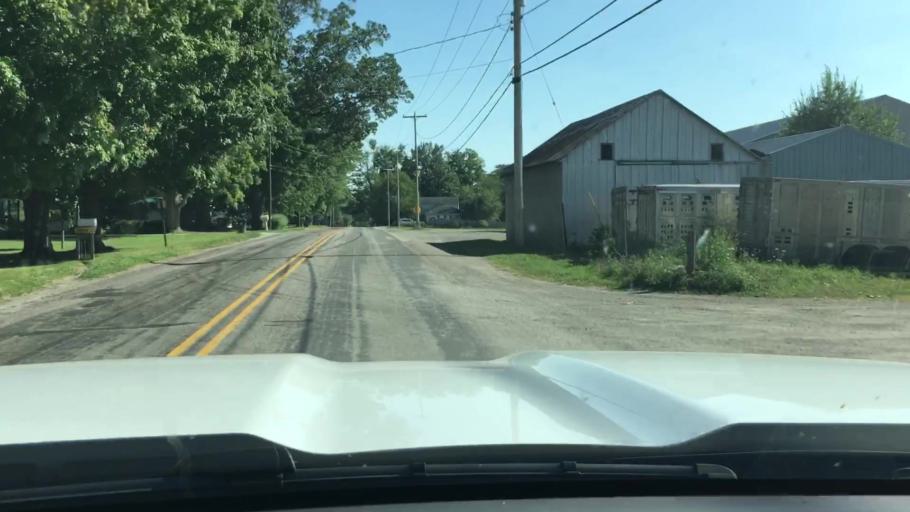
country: US
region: Michigan
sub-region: Muskegon County
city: Ravenna
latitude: 43.1948
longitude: -85.9368
